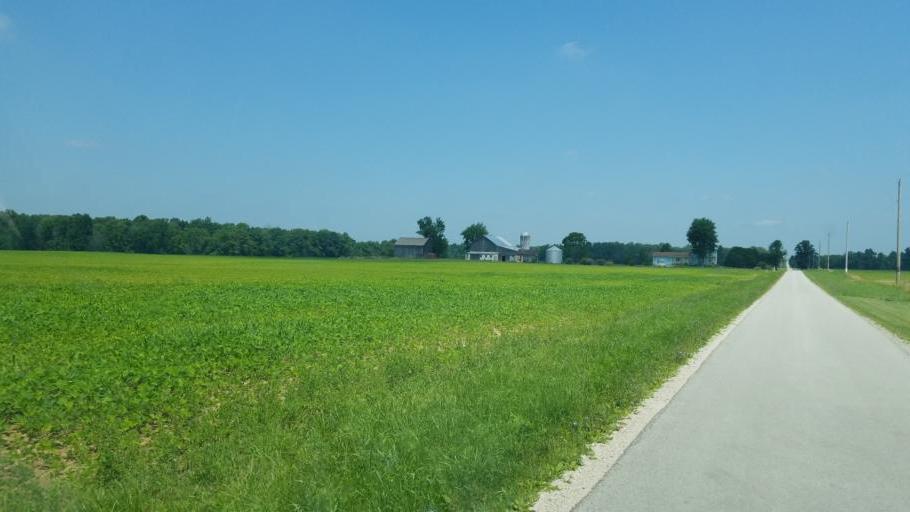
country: US
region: Ohio
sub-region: Sandusky County
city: Green Springs
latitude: 41.0668
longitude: -82.9769
